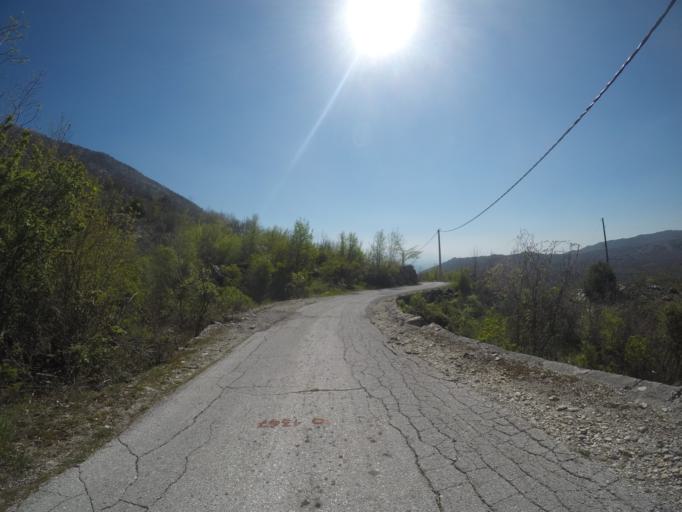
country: ME
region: Danilovgrad
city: Danilovgrad
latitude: 42.5300
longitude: 19.0272
